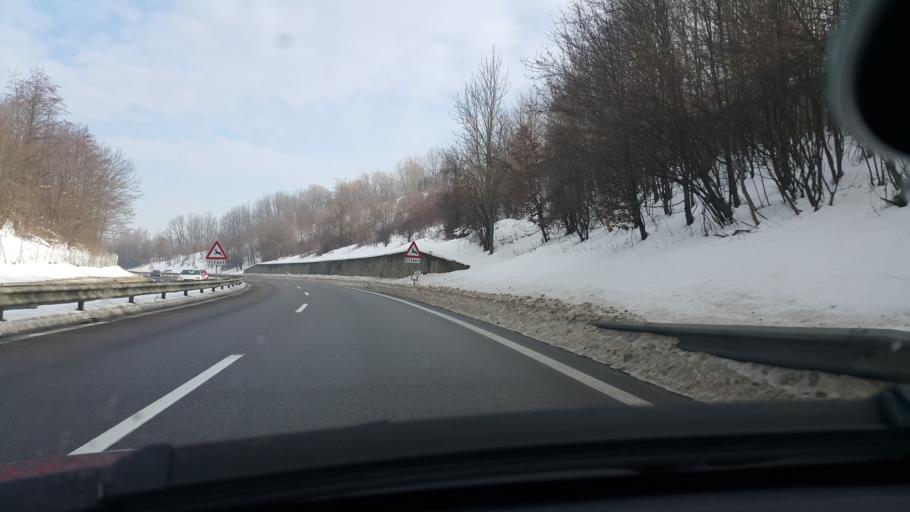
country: SI
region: Pesnica
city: Pesnica pri Mariboru
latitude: 46.5839
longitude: 15.6698
